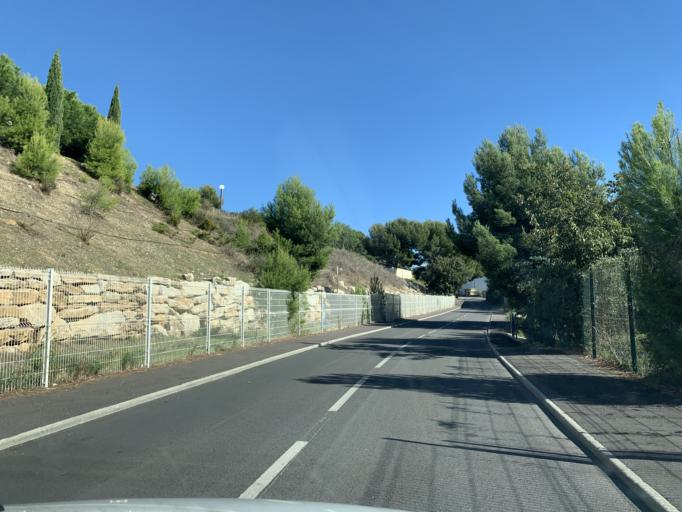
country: FR
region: Provence-Alpes-Cote d'Azur
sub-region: Departement des Bouches-du-Rhone
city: La Ciotat
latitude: 43.2052
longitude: 5.6008
